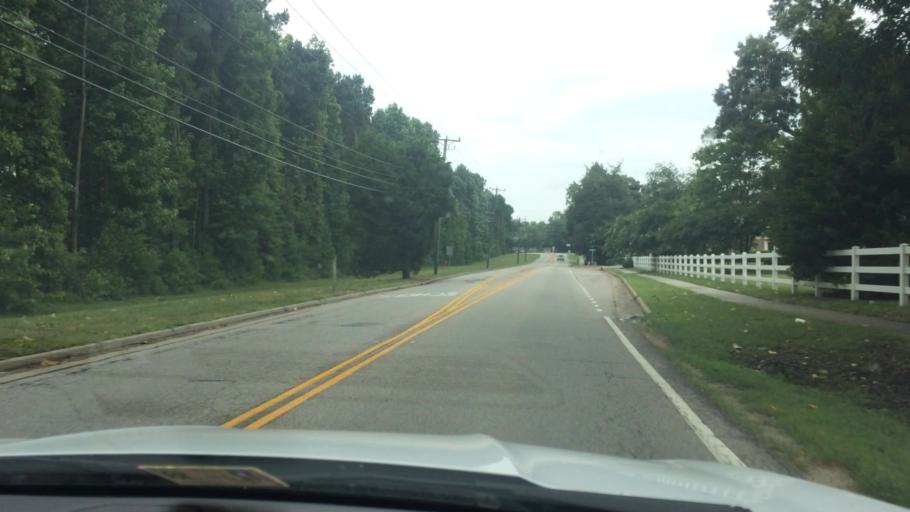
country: US
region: Virginia
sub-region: City of Williamsburg
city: Williamsburg
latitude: 37.2118
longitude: -76.6180
